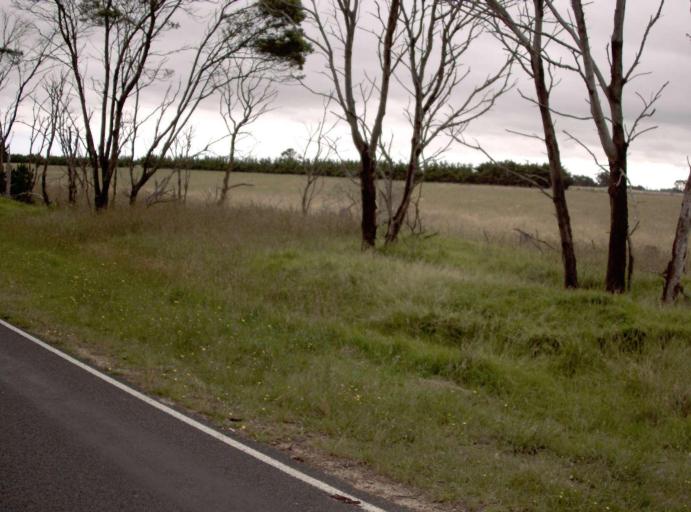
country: AU
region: Victoria
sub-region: Wellington
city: Sale
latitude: -38.5341
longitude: 146.8894
